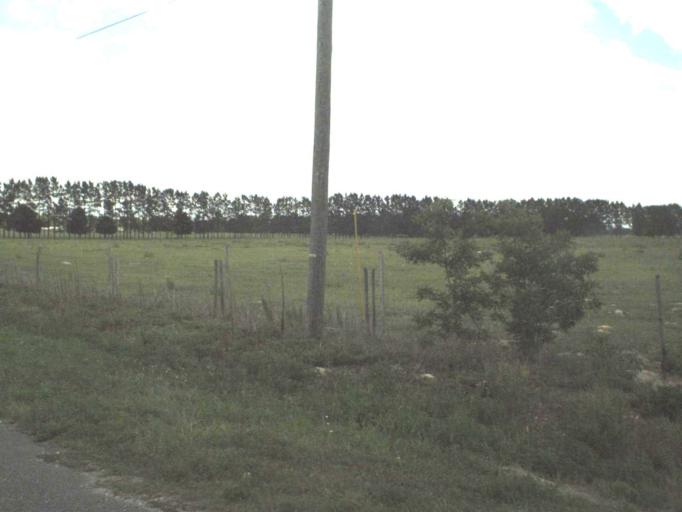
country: US
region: Florida
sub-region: Marion County
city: Belleview
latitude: 29.0855
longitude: -82.0535
